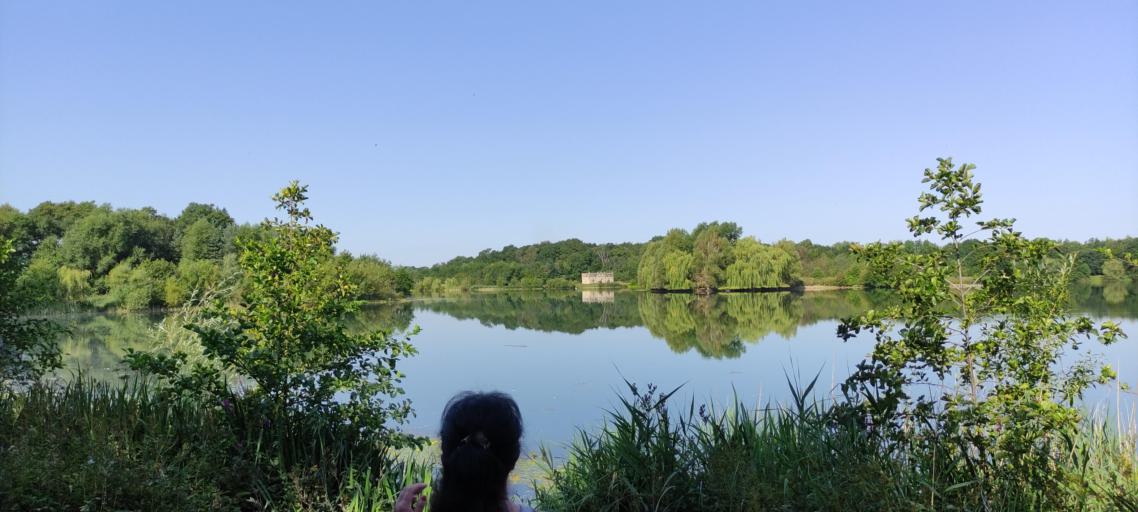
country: GB
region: England
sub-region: North Yorkshire
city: Catterick
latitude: 54.3700
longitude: -1.5790
